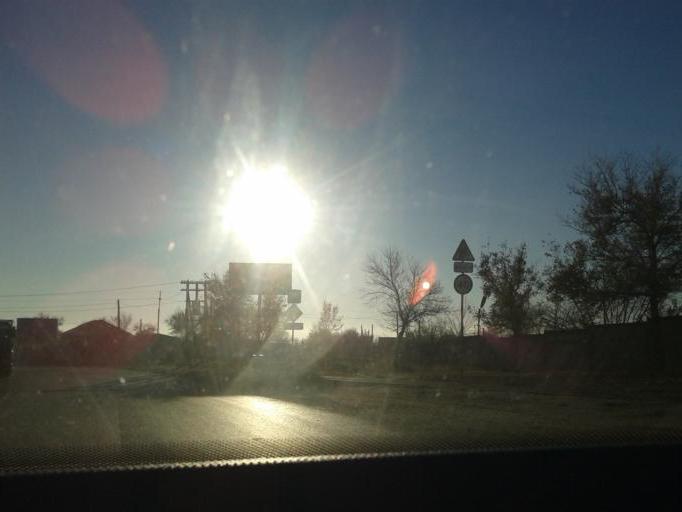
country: RU
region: Volgograd
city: Volgograd
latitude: 48.7029
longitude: 44.4543
